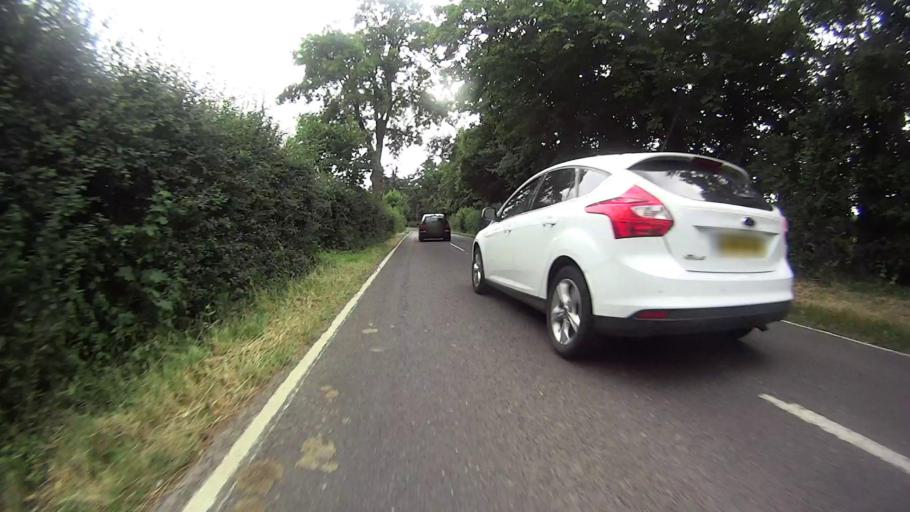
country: GB
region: England
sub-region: Surrey
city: Reigate
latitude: 51.1917
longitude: -0.2397
